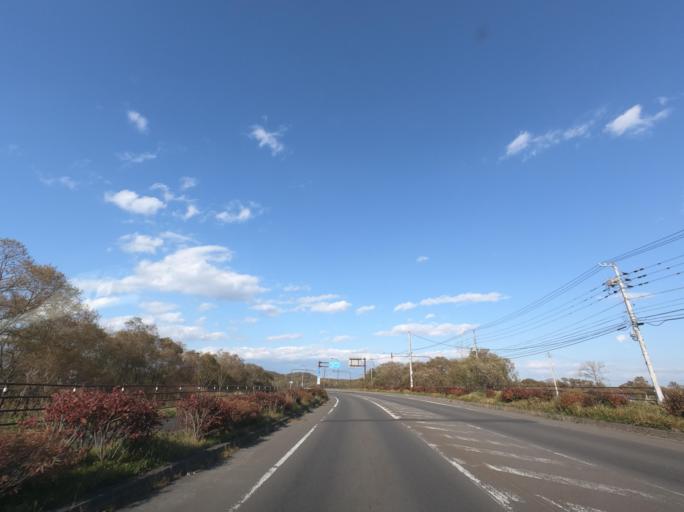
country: JP
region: Hokkaido
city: Kushiro
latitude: 43.0556
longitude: 144.2956
